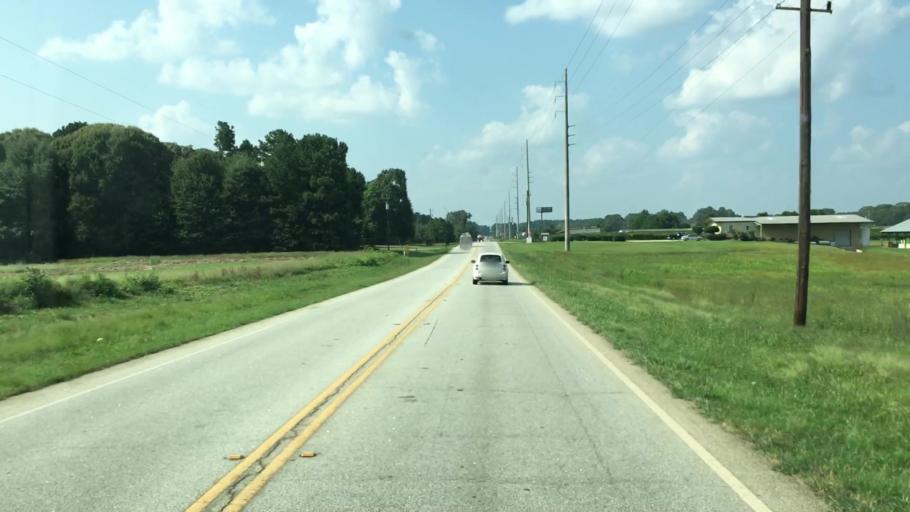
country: US
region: Georgia
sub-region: Walton County
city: Social Circle
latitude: 33.5916
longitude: -83.7485
